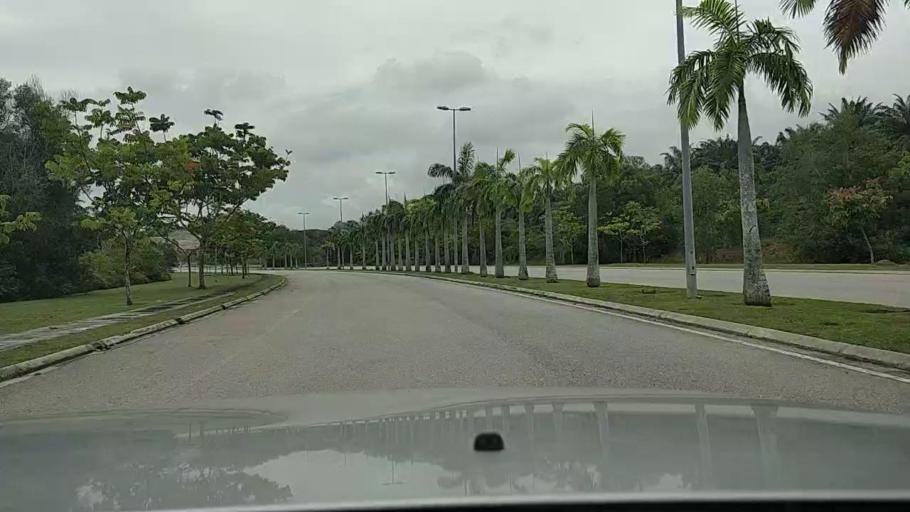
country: MY
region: Putrajaya
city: Putrajaya
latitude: 2.8997
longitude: 101.6469
